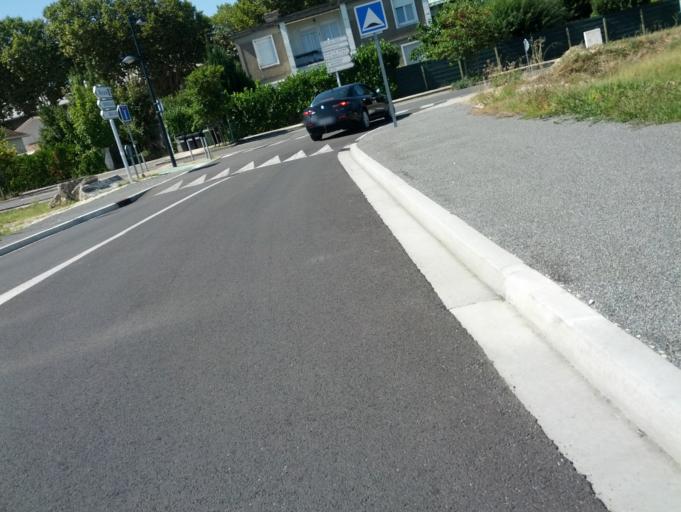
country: FR
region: Aquitaine
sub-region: Departement de la Gironde
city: Floirac
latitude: 44.8260
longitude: -0.5343
